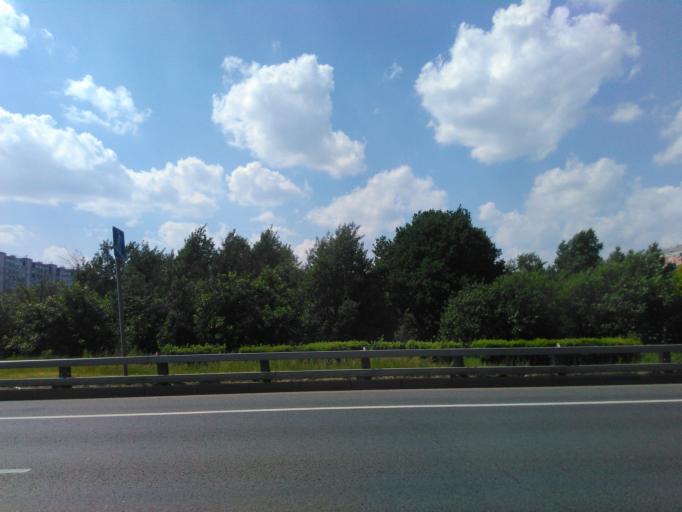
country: RU
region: Moscow
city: Ivanovskoye
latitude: 55.7626
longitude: 37.8427
